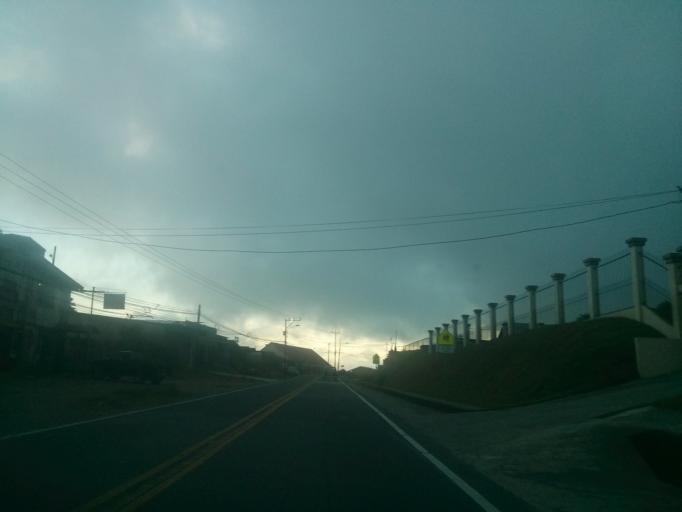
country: CR
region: Cartago
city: Cot
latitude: 9.8869
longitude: -83.8654
